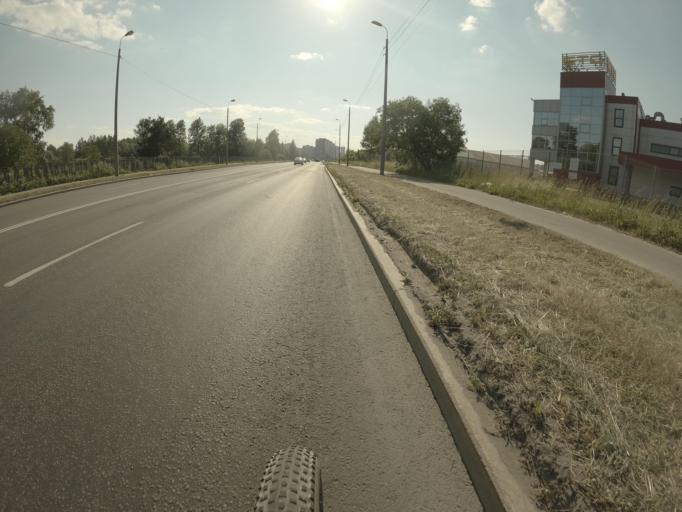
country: RU
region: St.-Petersburg
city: Obukhovo
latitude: 59.8527
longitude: 30.4337
